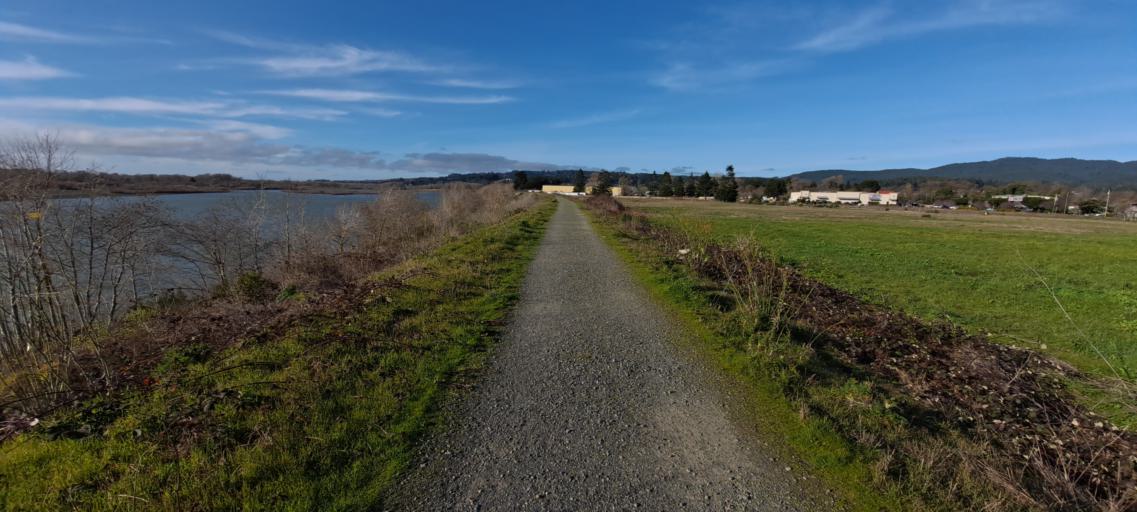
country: US
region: California
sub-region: Humboldt County
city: Fortuna
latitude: 40.5810
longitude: -124.1564
